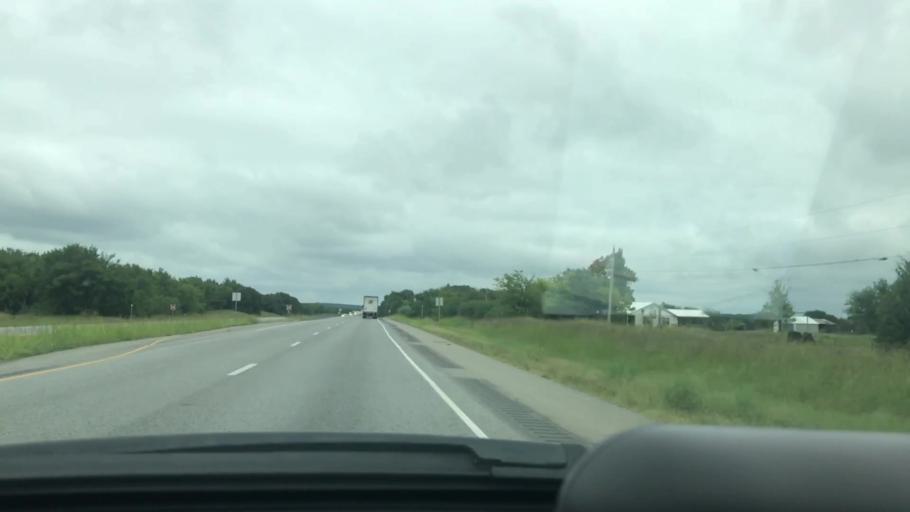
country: US
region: Oklahoma
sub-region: Pittsburg County
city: McAlester
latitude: 34.7608
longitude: -95.8903
